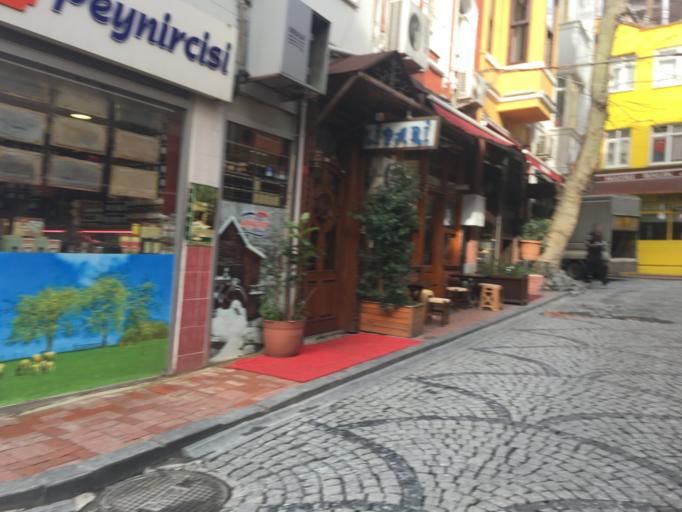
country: TR
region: Istanbul
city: UEskuedar
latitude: 41.0675
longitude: 29.0435
